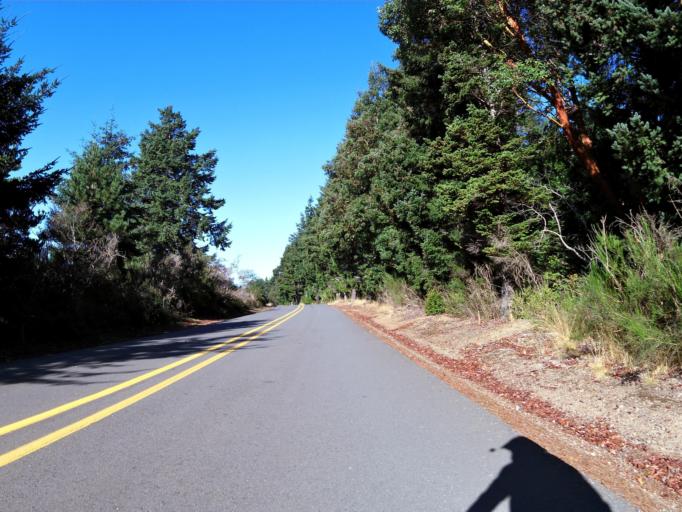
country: US
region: Oregon
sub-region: Coos County
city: Bandon
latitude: 43.0396
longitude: -124.4074
